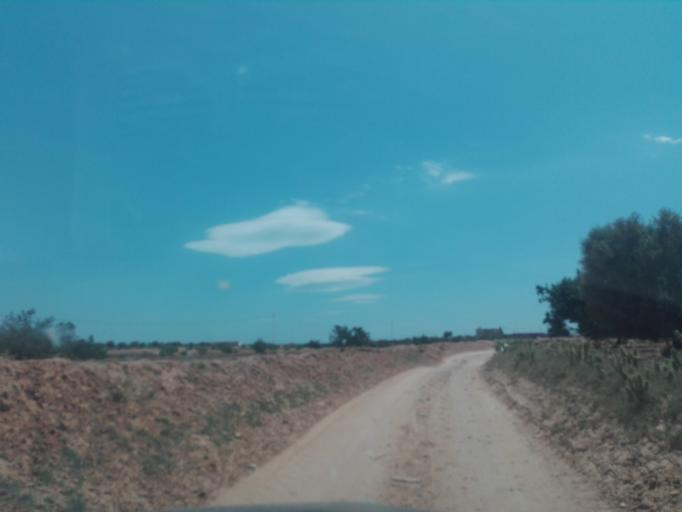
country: TN
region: Safaqis
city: Sfax
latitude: 34.6509
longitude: 10.5945
